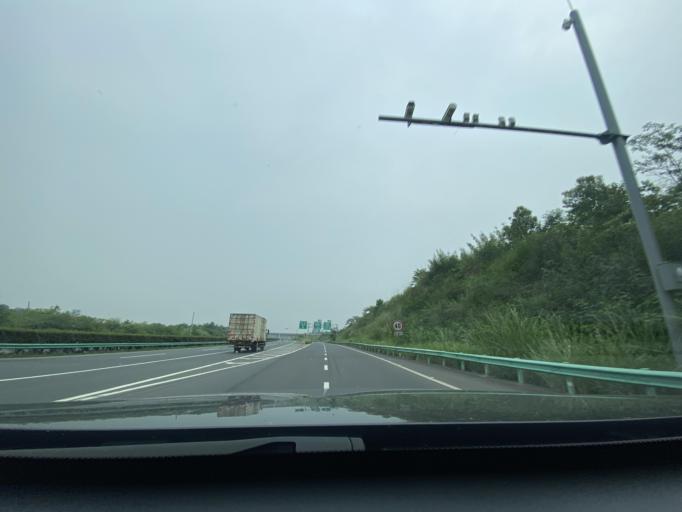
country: CN
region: Sichuan
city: Longquan
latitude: 30.3383
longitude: 104.1187
